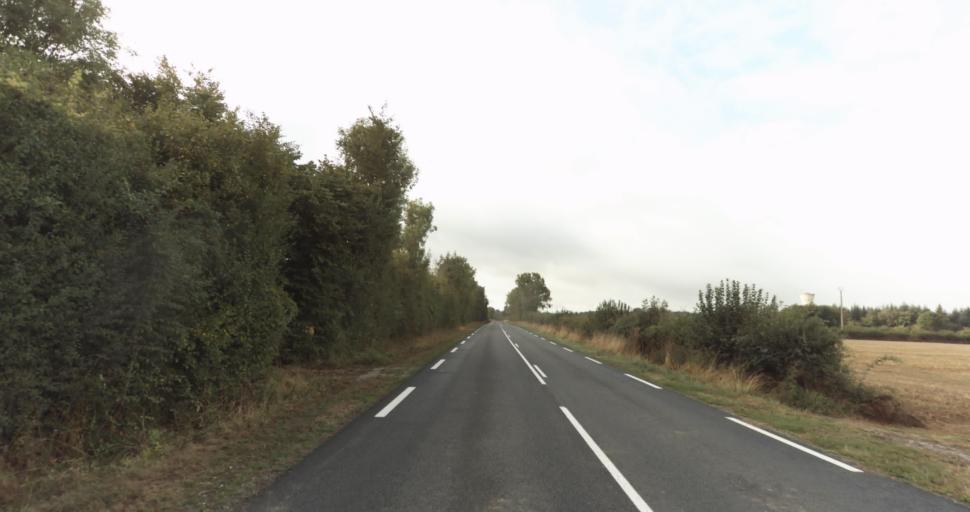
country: FR
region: Lower Normandy
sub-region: Departement de l'Orne
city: Vimoutiers
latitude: 48.9013
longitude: 0.2544
